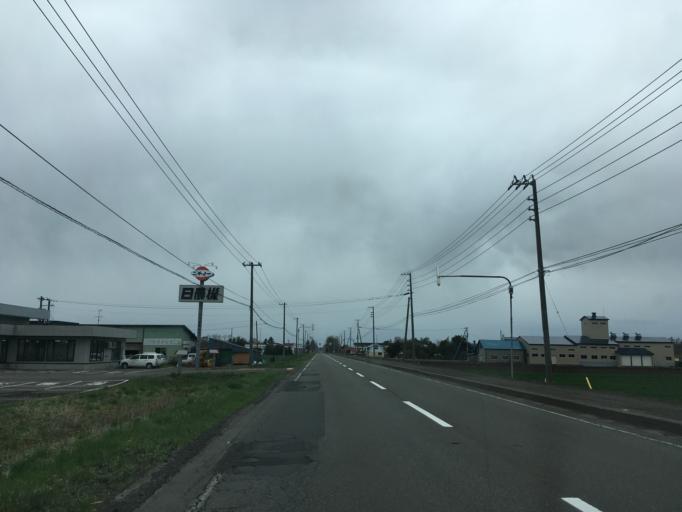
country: JP
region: Hokkaido
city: Chitose
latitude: 42.9352
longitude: 141.8059
